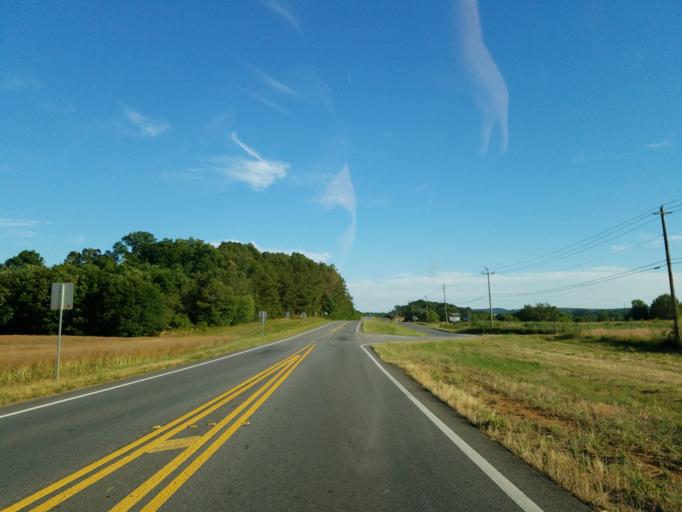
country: US
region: Georgia
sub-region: Bartow County
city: Adairsville
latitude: 34.4001
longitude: -84.9347
